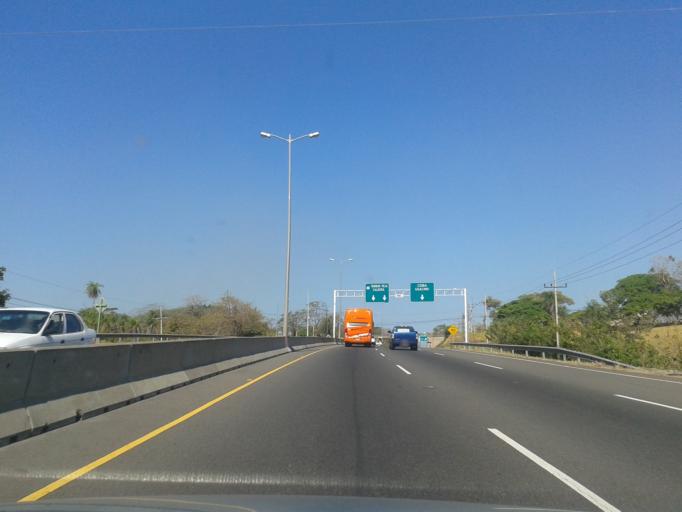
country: CR
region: Alajuela
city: Orotina
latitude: 9.8913
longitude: -84.6099
